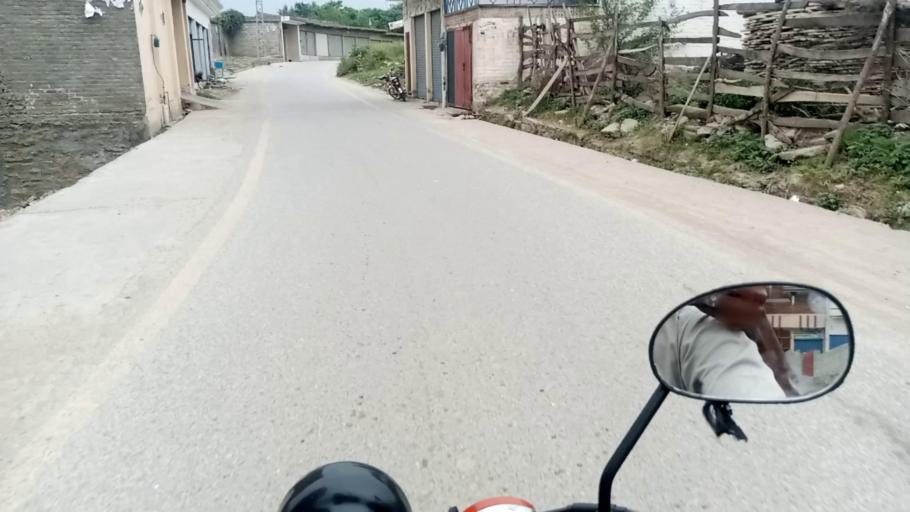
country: PK
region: Khyber Pakhtunkhwa
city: Mingora
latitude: 34.7587
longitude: 72.3773
